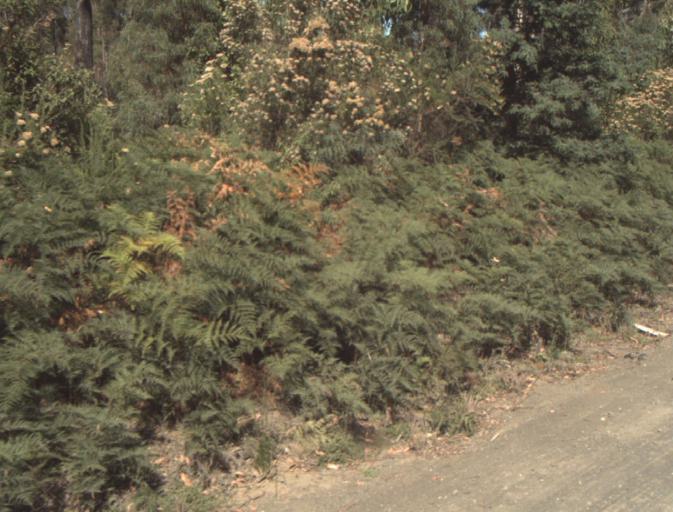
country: AU
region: Tasmania
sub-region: Launceston
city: Mayfield
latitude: -41.3357
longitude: 147.1999
